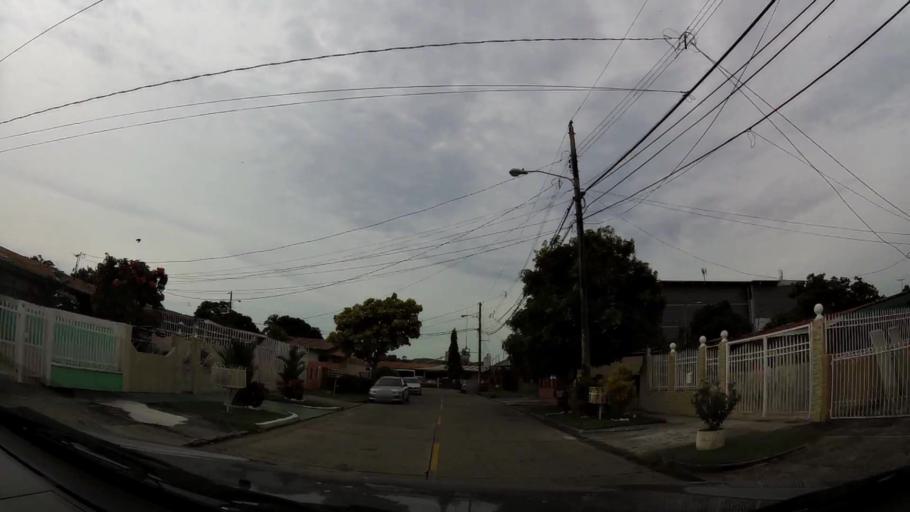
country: PA
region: Panama
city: San Miguelito
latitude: 9.0378
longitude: -79.4777
